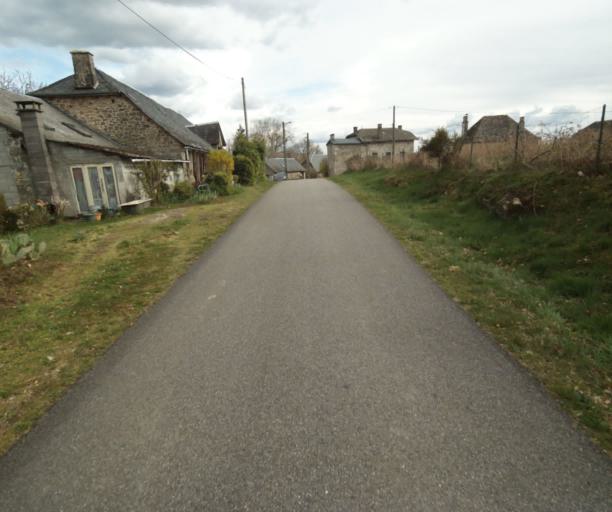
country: FR
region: Limousin
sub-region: Departement de la Correze
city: Argentat
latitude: 45.2142
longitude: 1.9592
